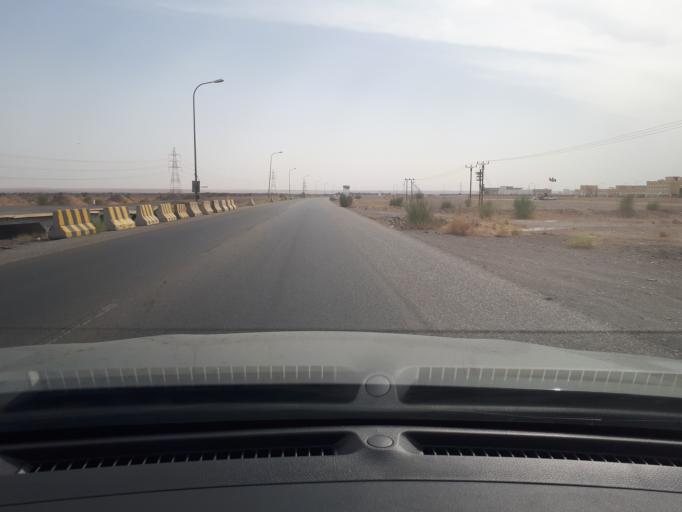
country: OM
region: Ash Sharqiyah
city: Badiyah
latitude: 22.4713
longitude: 58.8971
